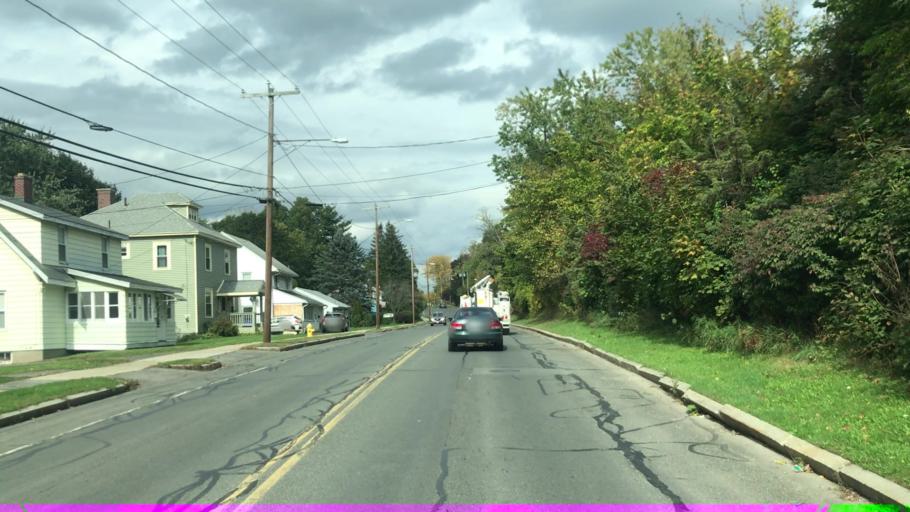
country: US
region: Massachusetts
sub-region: Berkshire County
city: Pittsfield
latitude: 42.4637
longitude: -73.2464
